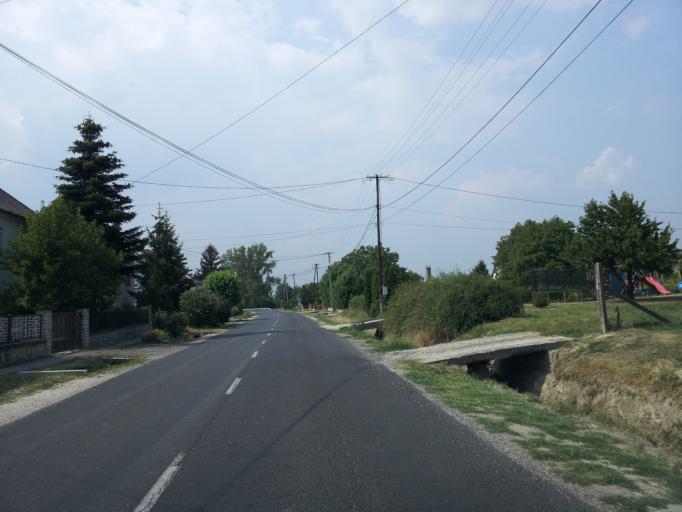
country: HU
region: Gyor-Moson-Sopron
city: Pannonhalma
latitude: 47.5552
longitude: 17.7463
